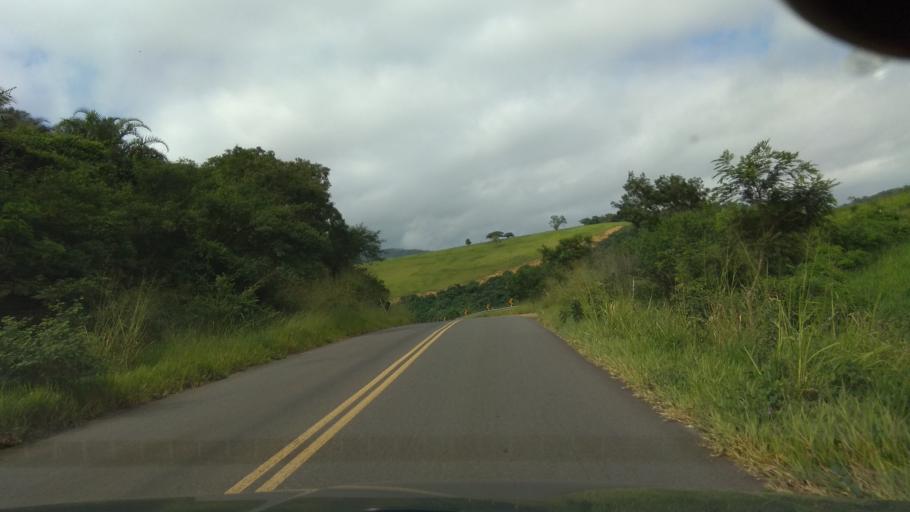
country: BR
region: Bahia
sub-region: Ubaira
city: Ubaira
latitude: -13.2614
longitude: -39.7099
